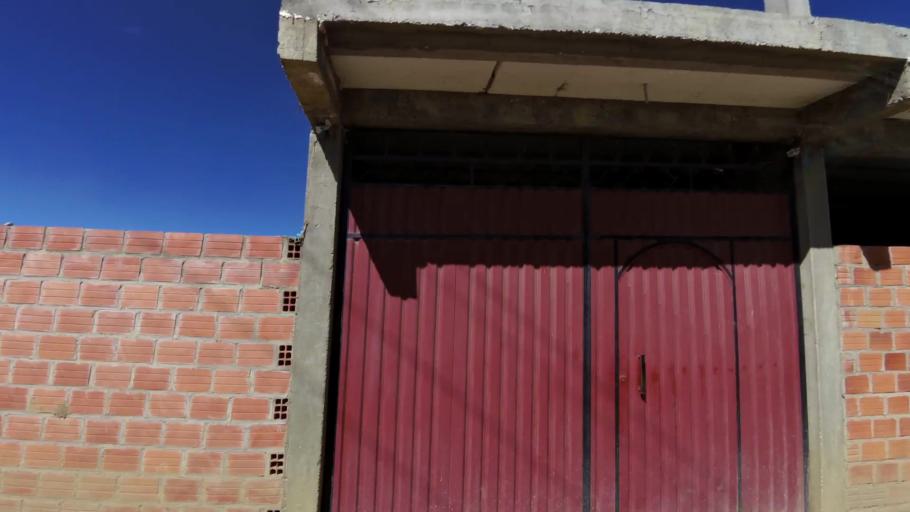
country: BO
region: La Paz
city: La Paz
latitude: -16.5728
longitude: -68.2205
